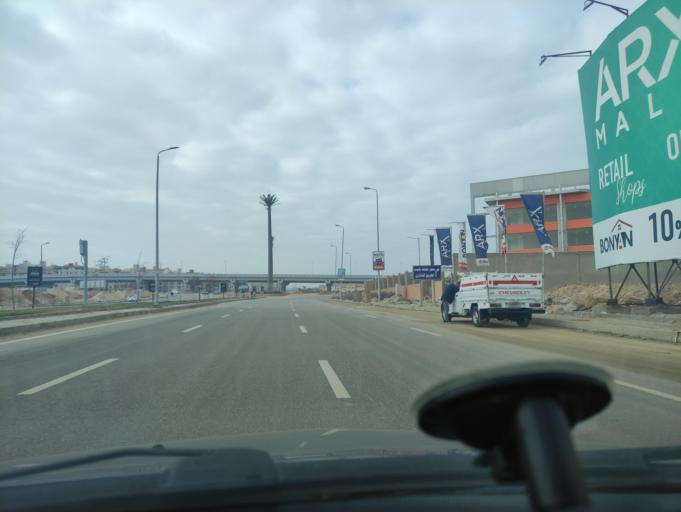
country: EG
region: Muhafazat al Qalyubiyah
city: Al Khankah
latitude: 30.0448
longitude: 31.5251
